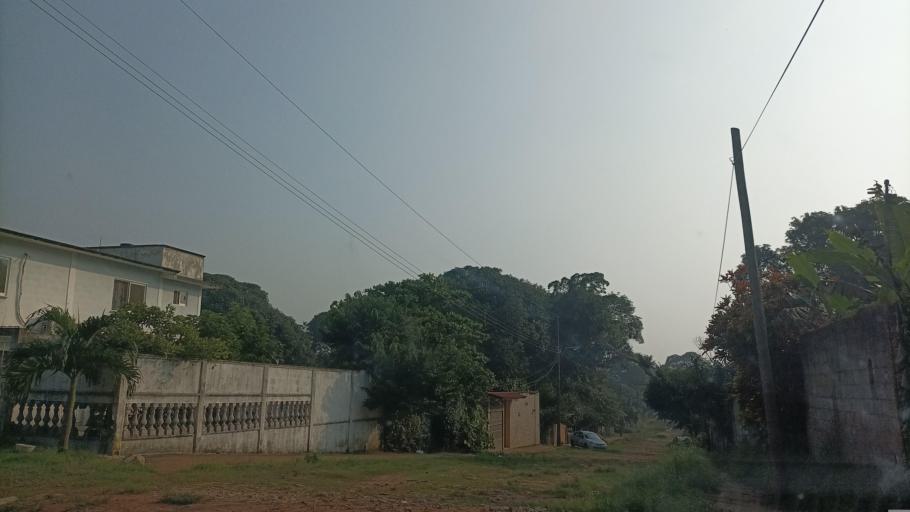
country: MX
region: Veracruz
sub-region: Cosoleacaque
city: Residencial las Olas
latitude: 18.0977
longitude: -94.5708
